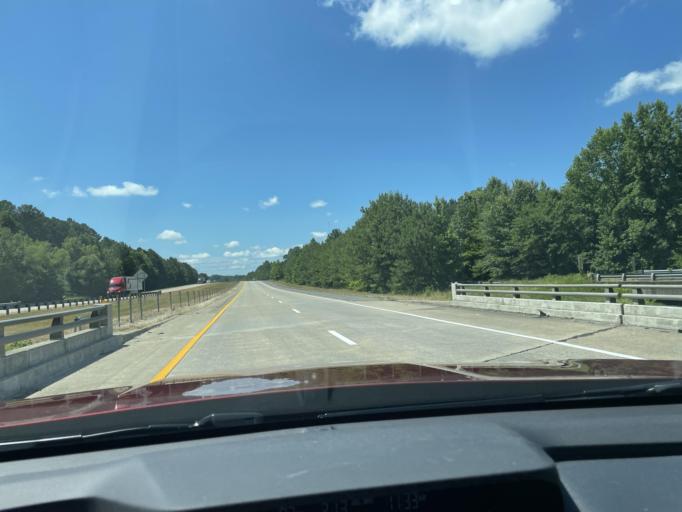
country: US
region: Arkansas
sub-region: Jefferson County
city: Redfield
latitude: 34.4889
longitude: -92.2087
